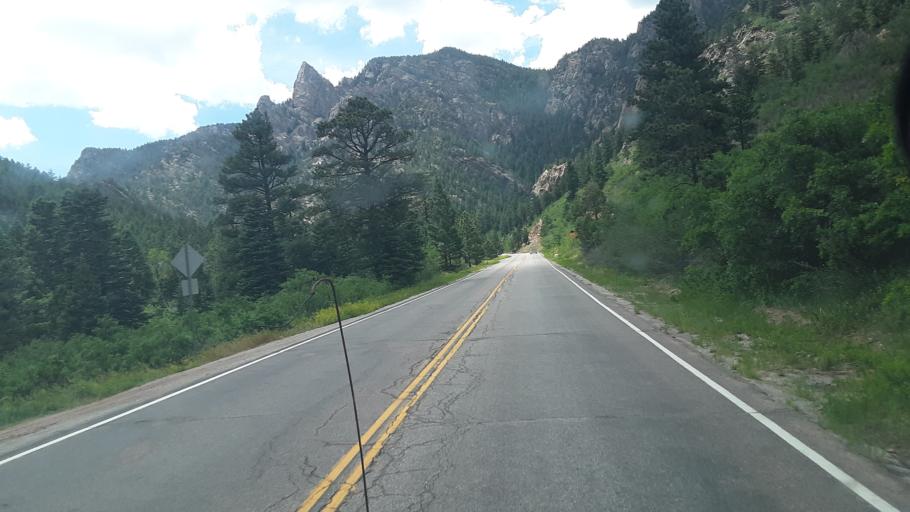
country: US
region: Colorado
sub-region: Fremont County
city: Florence
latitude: 38.1721
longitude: -105.1635
